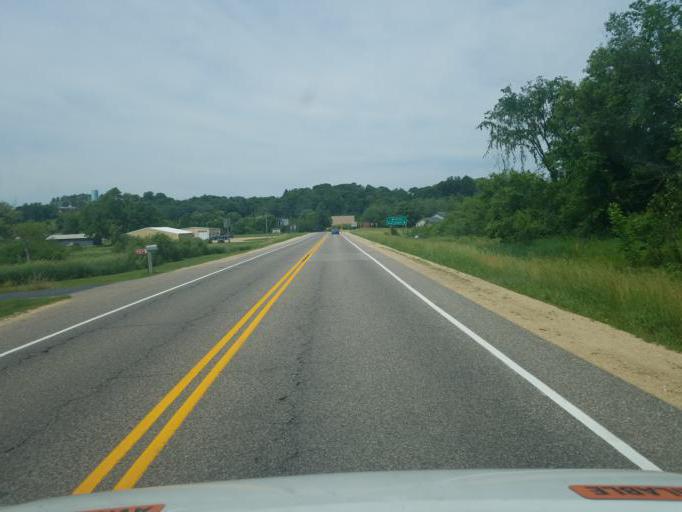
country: US
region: Wisconsin
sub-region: Juneau County
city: Elroy
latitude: 43.7605
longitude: -90.2692
